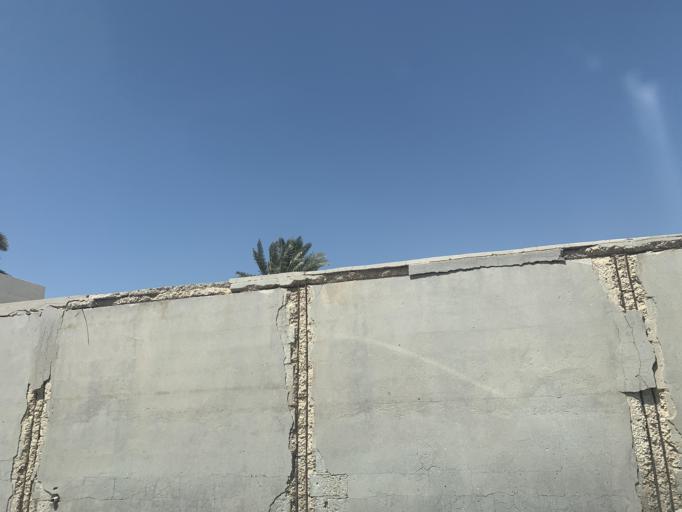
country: BH
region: Manama
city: Jidd Hafs
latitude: 26.2283
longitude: 50.5013
